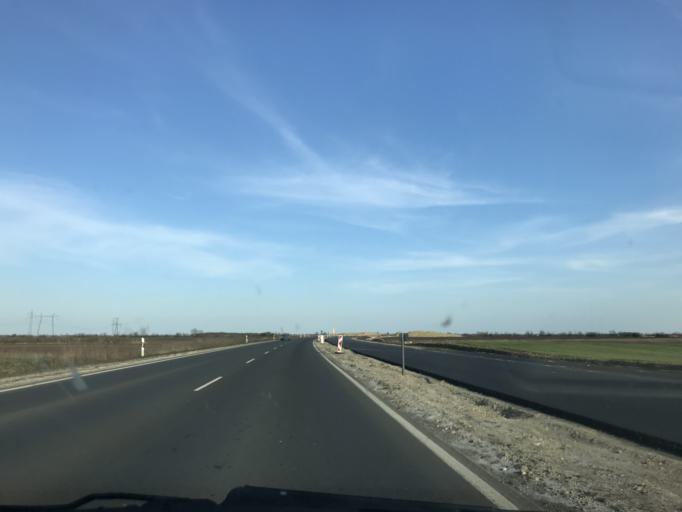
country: HU
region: Pest
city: Abony
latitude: 47.2131
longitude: 20.0572
